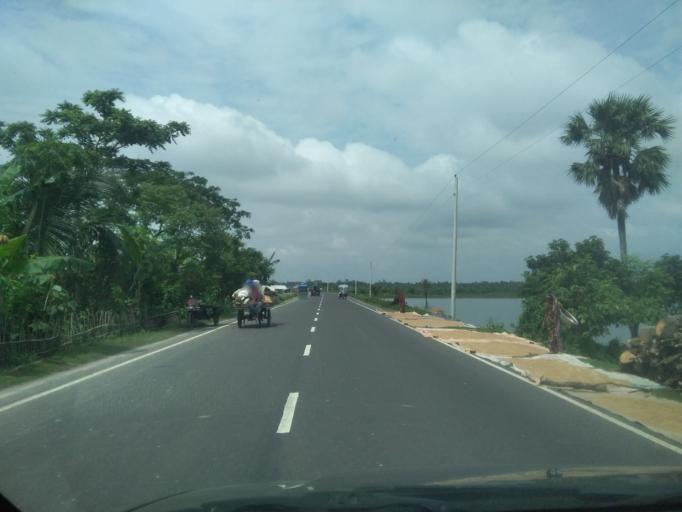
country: BD
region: Khulna
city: Kesabpur
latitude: 22.7885
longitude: 89.2165
